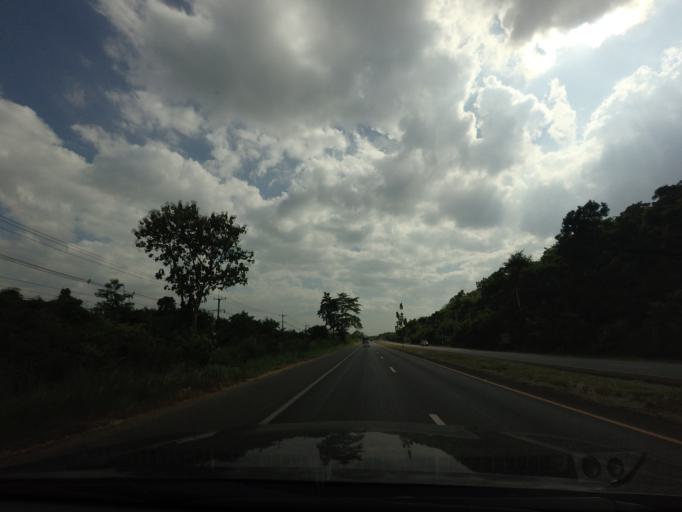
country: TH
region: Lop Buri
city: Chai Badan
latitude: 15.2933
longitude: 101.1284
